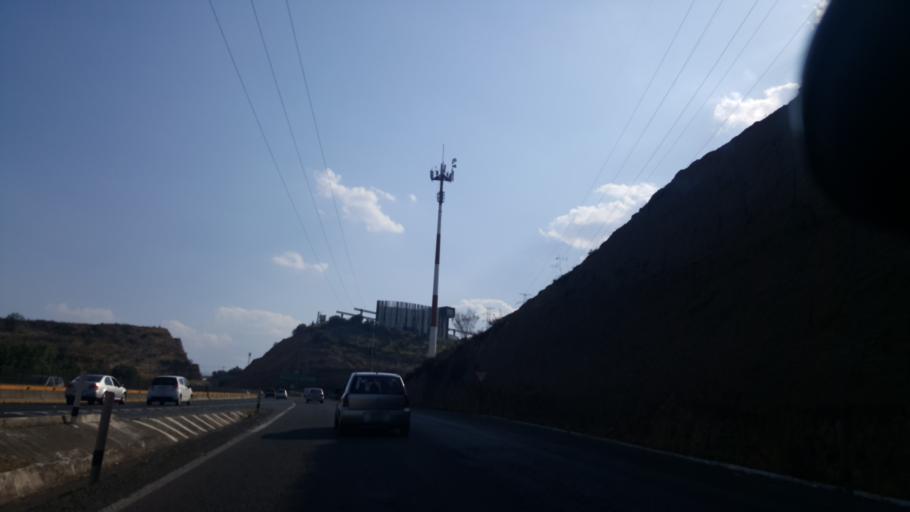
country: MX
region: Mexico
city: Ciudad Lopez Mateos
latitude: 19.5801
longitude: -99.2694
